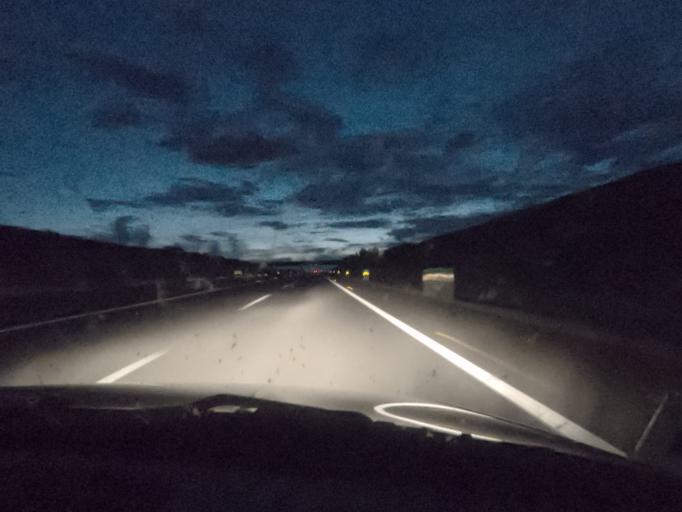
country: ES
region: Extremadura
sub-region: Provincia de Caceres
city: Riolobos
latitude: 39.9736
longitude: -6.3435
